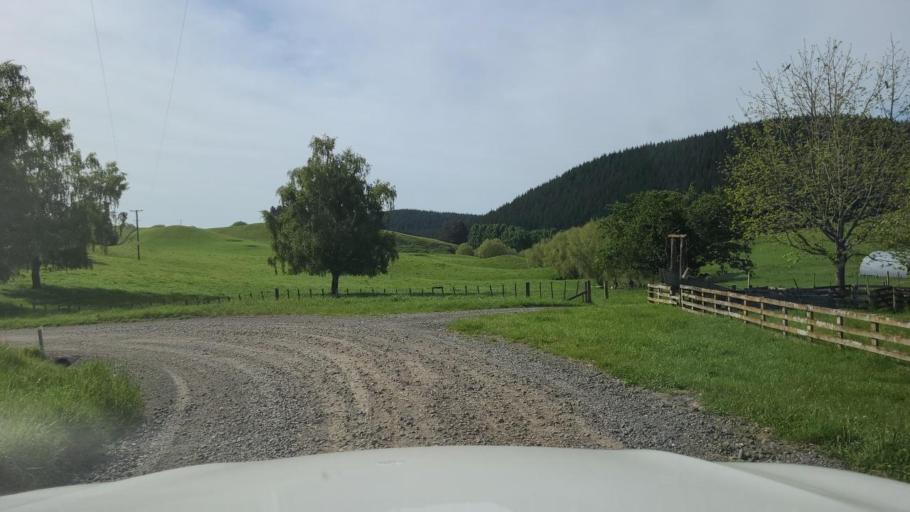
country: NZ
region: Hawke's Bay
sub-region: Napier City
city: Taradale
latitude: -39.3504
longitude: 176.6783
